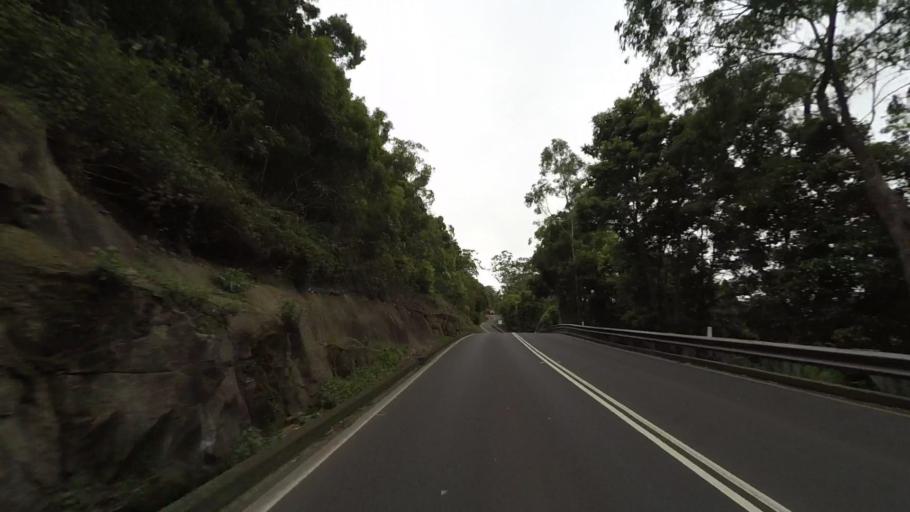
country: AU
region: New South Wales
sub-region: Wollongong
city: Bulli
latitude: -34.3163
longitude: 150.8952
